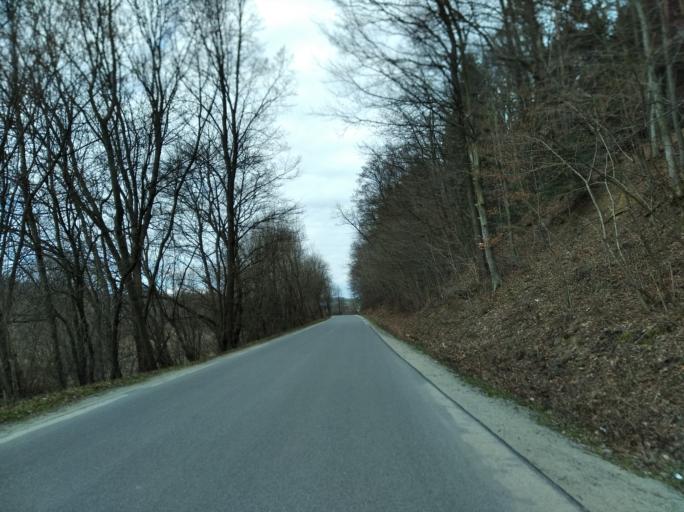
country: PL
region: Subcarpathian Voivodeship
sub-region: Powiat strzyzowski
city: Frysztak
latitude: 49.8521
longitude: 21.6244
